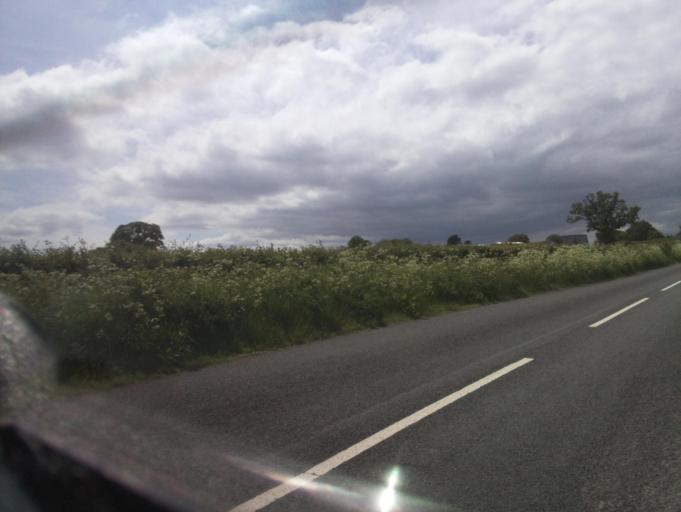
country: GB
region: England
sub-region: Herefordshire
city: Llanrothal
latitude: 51.8885
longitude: -2.7517
